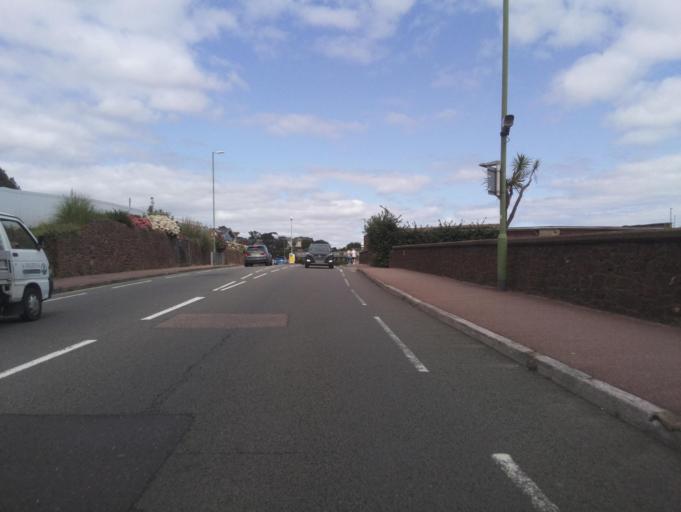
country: GB
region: England
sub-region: Borough of Torbay
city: Paignton
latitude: 50.4549
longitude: -3.5458
